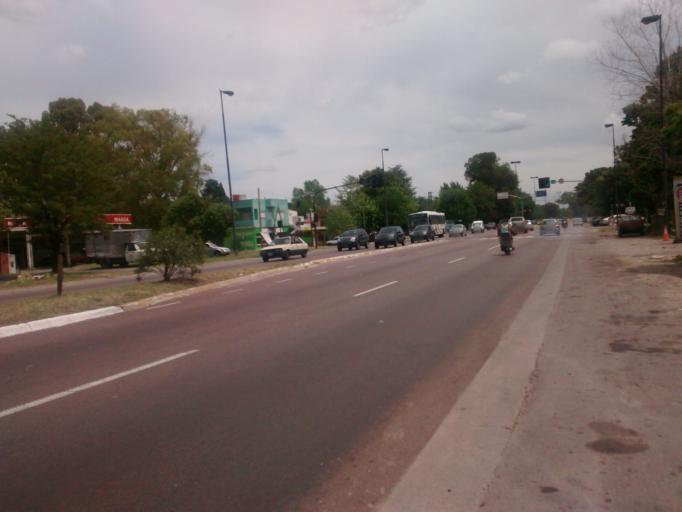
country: AR
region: Buenos Aires
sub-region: Partido de La Plata
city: La Plata
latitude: -34.8618
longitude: -58.0577
